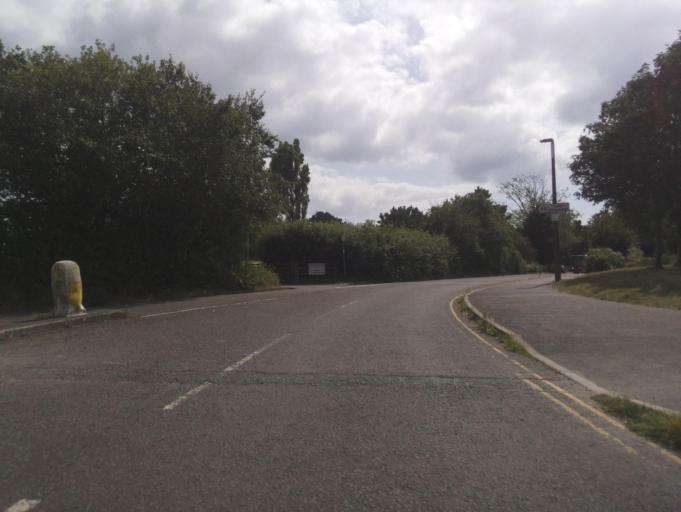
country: GB
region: England
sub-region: Poole
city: Poole
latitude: 50.7148
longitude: -1.9715
